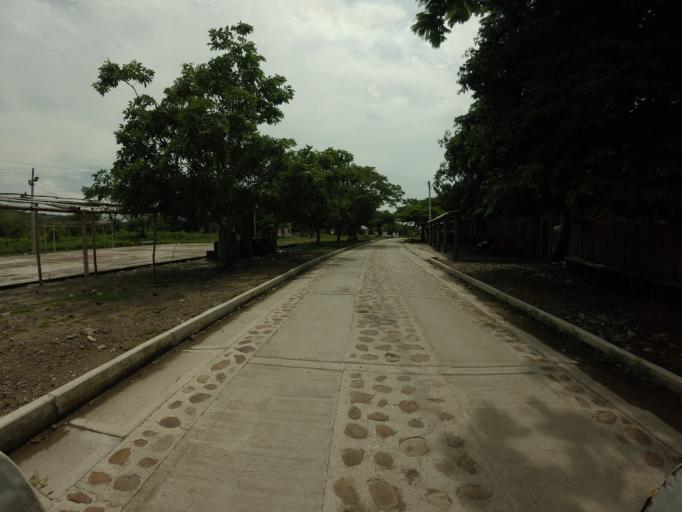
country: CO
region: Tolima
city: Natagaima
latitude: 3.4609
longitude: -75.1394
